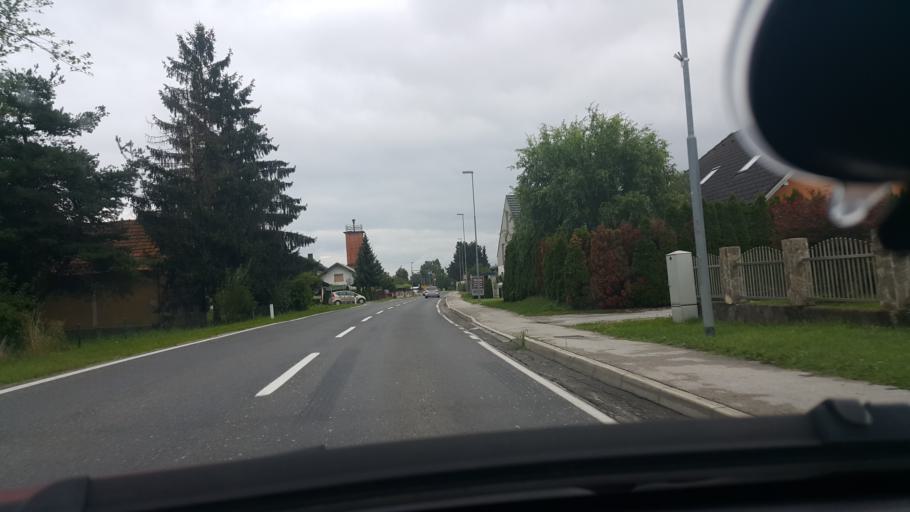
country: SI
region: Gorisnica
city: Gorisnica
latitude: 46.4131
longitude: 16.0108
